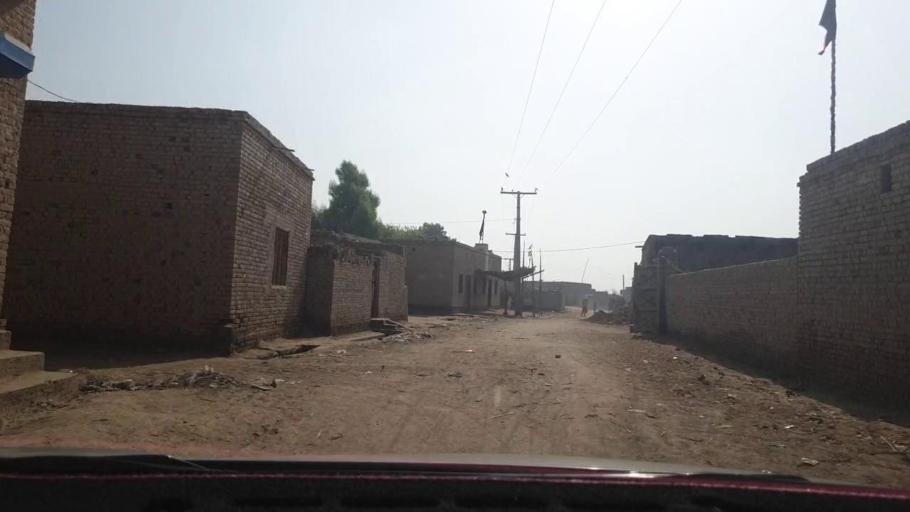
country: PK
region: Sindh
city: Nasirabad
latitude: 27.4384
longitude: 67.9556
